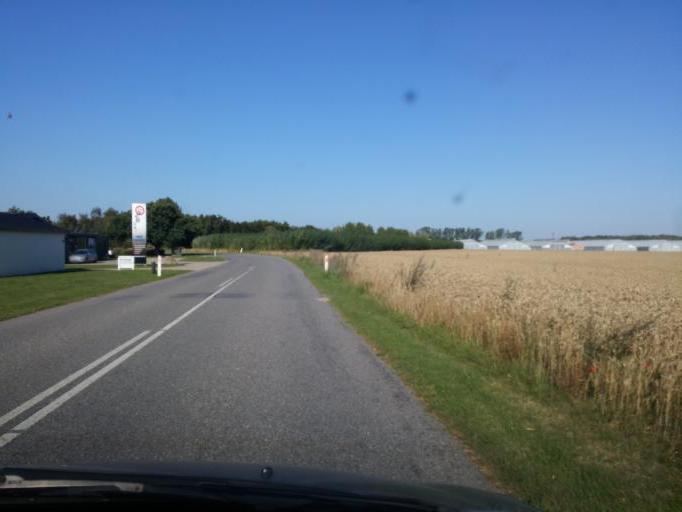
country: DK
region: South Denmark
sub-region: Kerteminde Kommune
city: Munkebo
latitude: 55.4059
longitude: 10.5462
